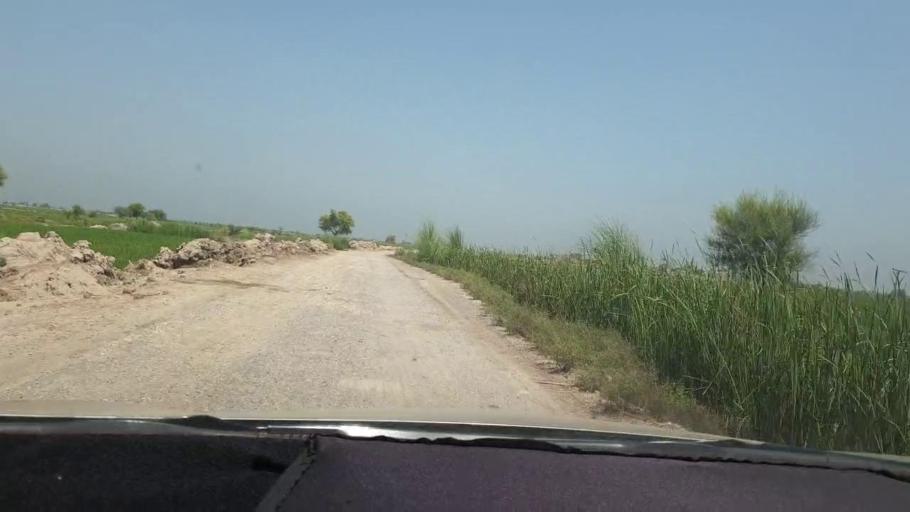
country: PK
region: Sindh
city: Shahdadkot
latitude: 27.8367
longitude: 67.9970
